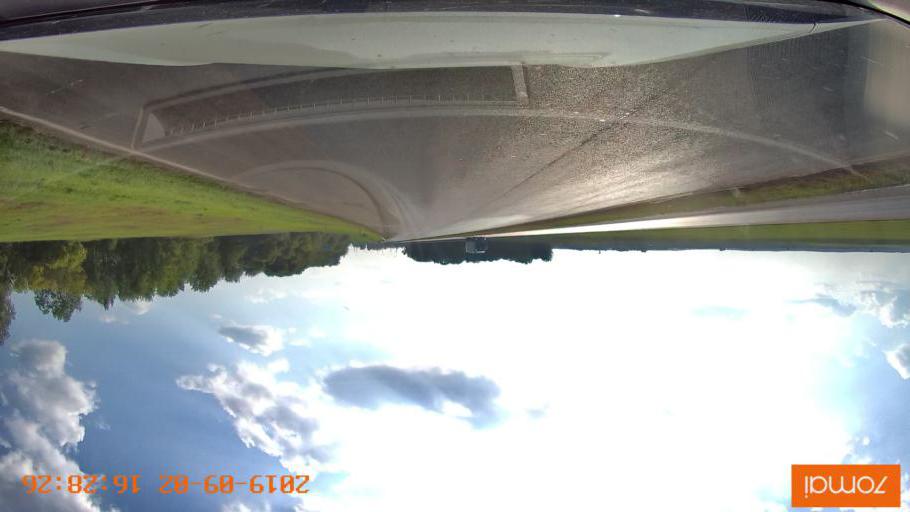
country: BY
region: Minsk
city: Smilavichy
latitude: 53.7641
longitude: 28.1768
